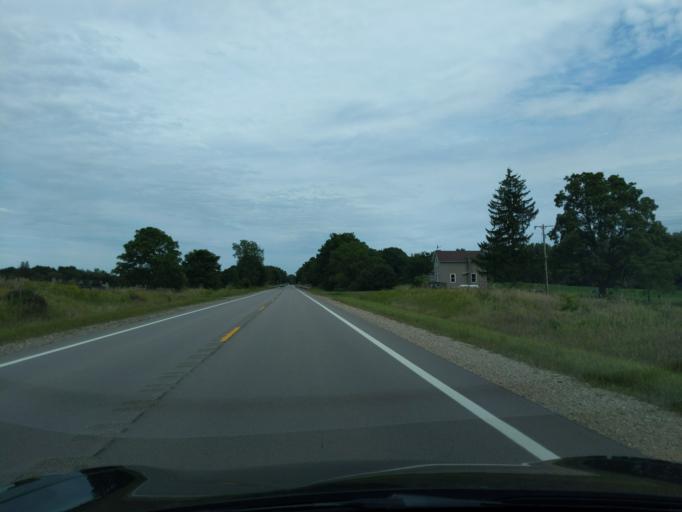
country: US
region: Michigan
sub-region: Barry County
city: Nashville
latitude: 42.5673
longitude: -85.0271
